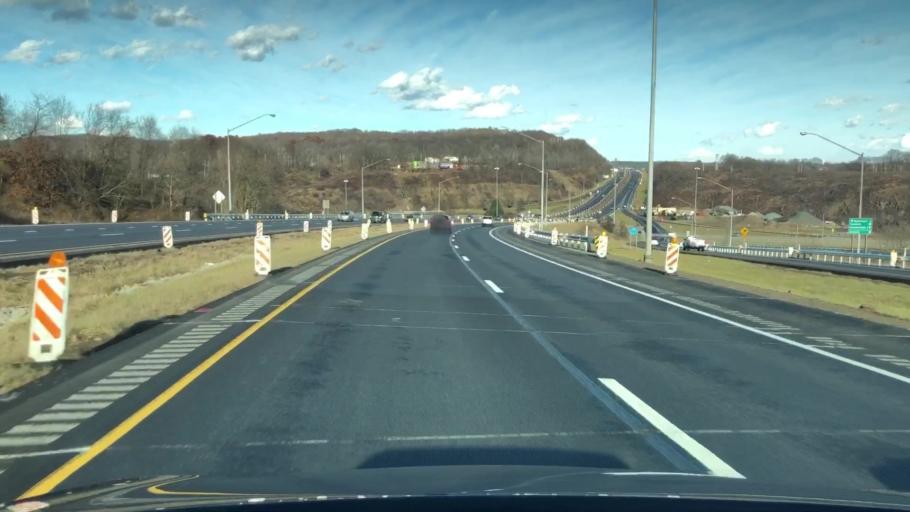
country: US
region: Pennsylvania
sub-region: Allegheny County
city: Tarentum
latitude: 40.6106
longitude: -79.7609
